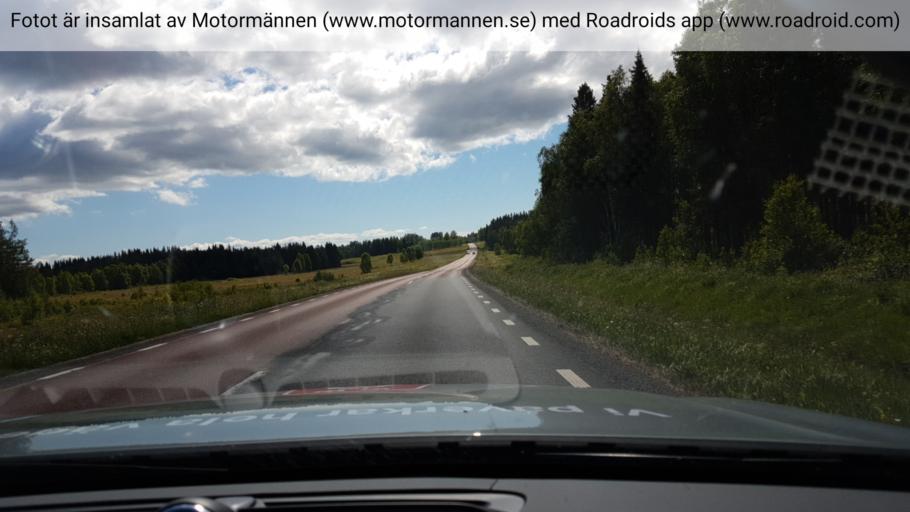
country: SE
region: Jaemtland
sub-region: Stroemsunds Kommun
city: Stroemsund
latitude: 63.7468
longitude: 15.4945
